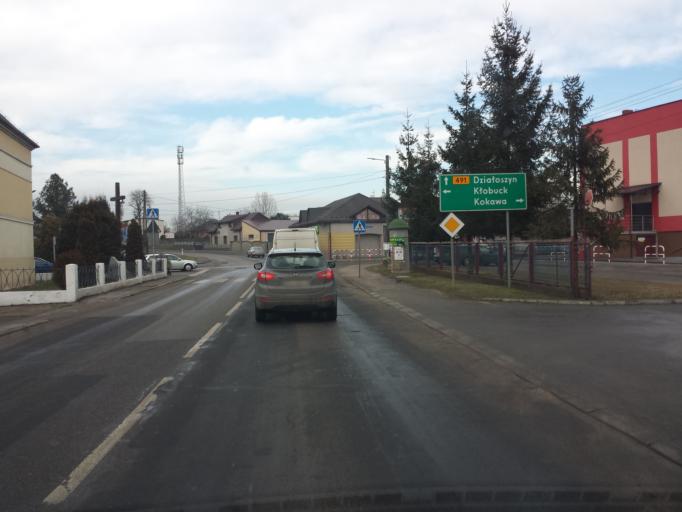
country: PL
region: Silesian Voivodeship
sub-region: Powiat klobucki
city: Kamyk
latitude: 50.9011
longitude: 19.0291
